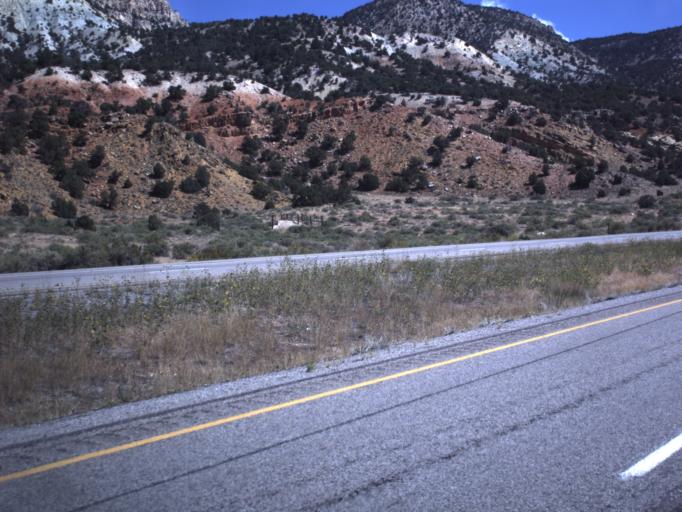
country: US
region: Utah
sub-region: Sevier County
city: Salina
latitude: 38.9330
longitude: -111.8012
